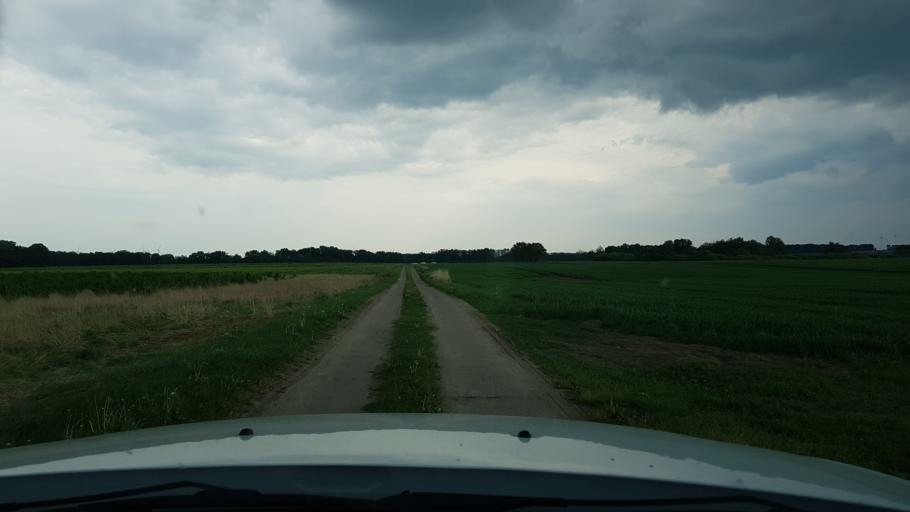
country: PL
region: West Pomeranian Voivodeship
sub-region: Powiat stargardzki
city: Stara Dabrowa
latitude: 53.3654
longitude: 15.1830
